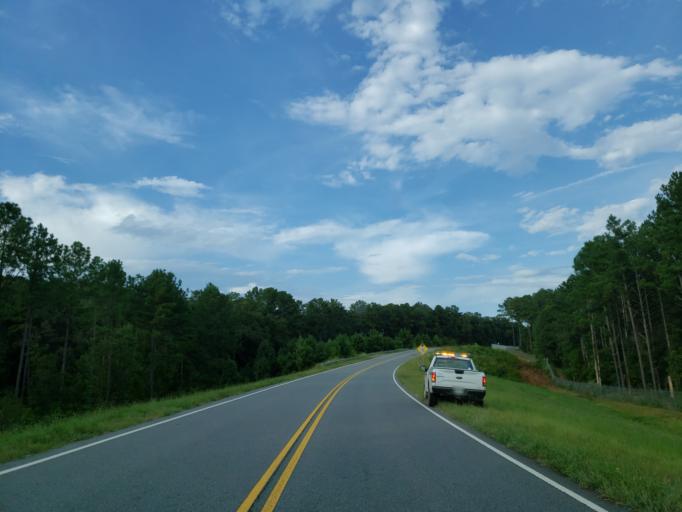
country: US
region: Georgia
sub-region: Bartow County
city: Euharlee
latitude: 34.1349
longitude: -84.9375
